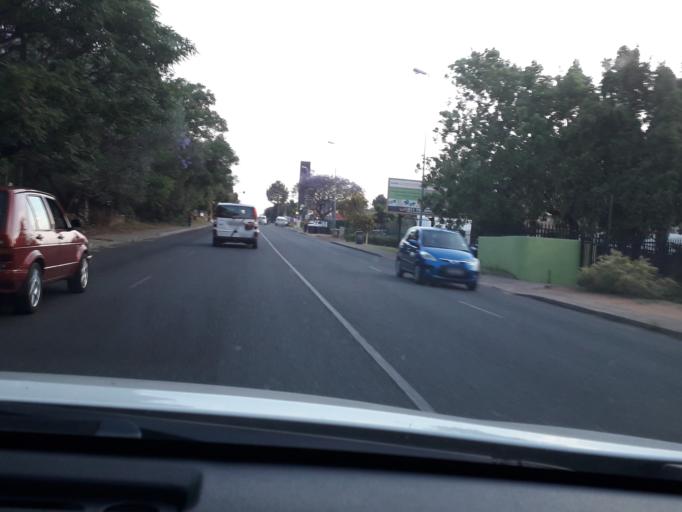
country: ZA
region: Gauteng
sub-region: City of Johannesburg Metropolitan Municipality
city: Johannesburg
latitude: -26.1095
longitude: 28.0010
